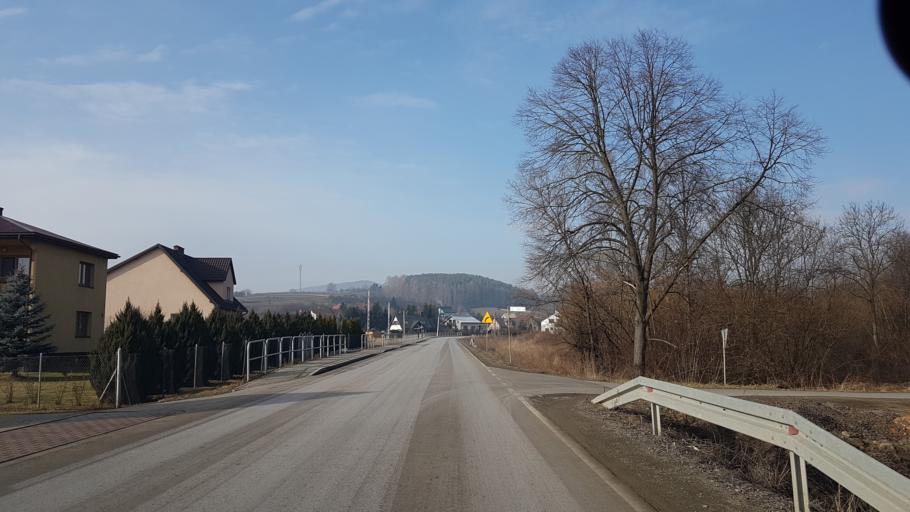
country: PL
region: Lesser Poland Voivodeship
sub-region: Powiat nowosadecki
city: Olszana
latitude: 49.5957
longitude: 20.5315
